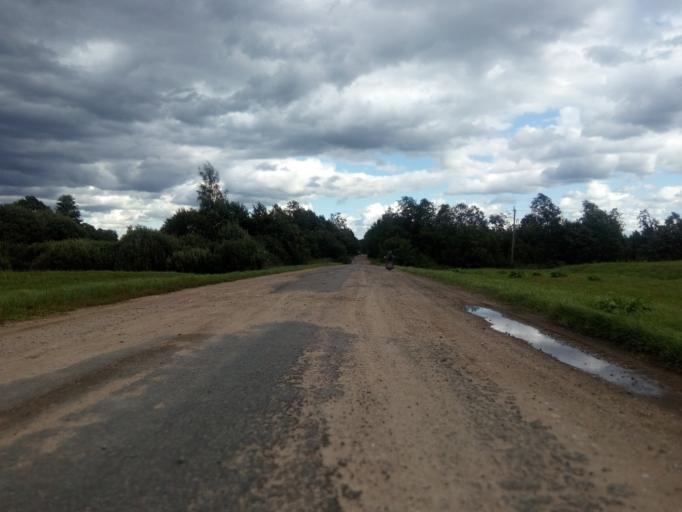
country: BY
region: Vitebsk
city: Dzisna
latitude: 55.7082
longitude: 28.3128
